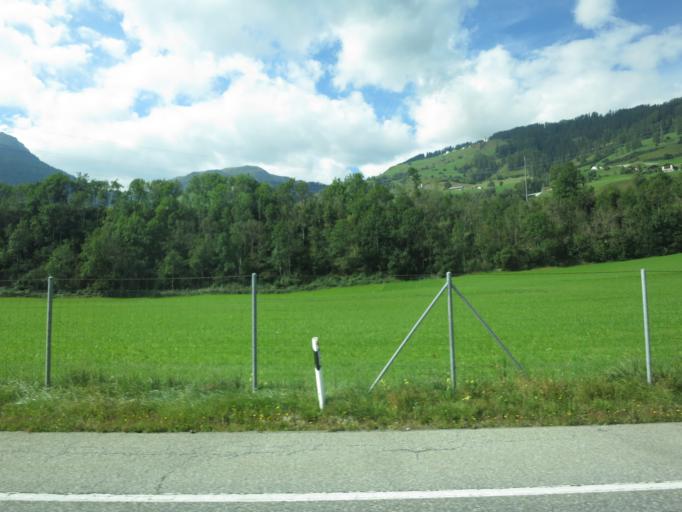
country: CH
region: Grisons
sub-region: Hinterrhein District
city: Thusis
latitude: 46.6312
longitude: 9.4386
